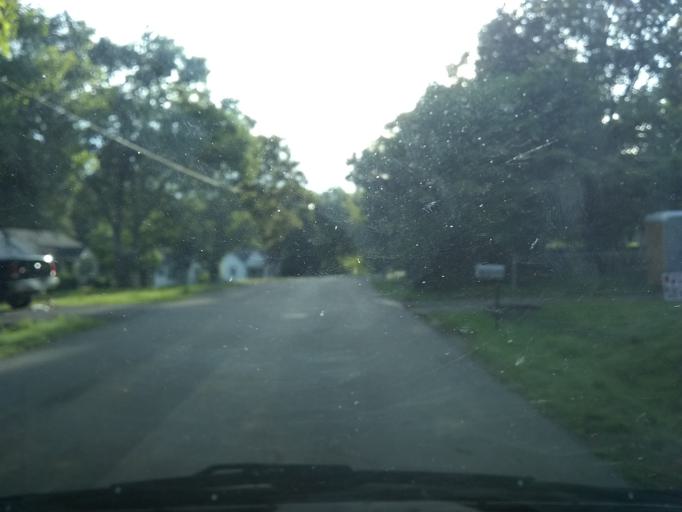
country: US
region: Tennessee
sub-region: Davidson County
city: Nashville
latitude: 36.1304
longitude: -86.7020
